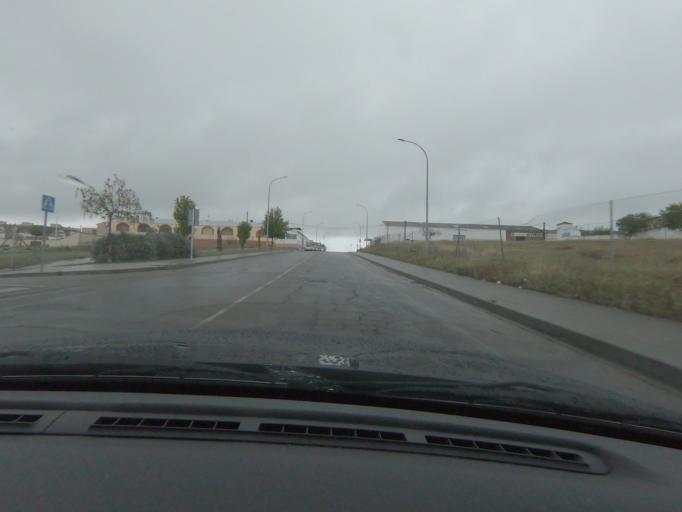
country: ES
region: Extremadura
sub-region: Provincia de Badajoz
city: Merida
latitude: 38.9262
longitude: -6.3378
